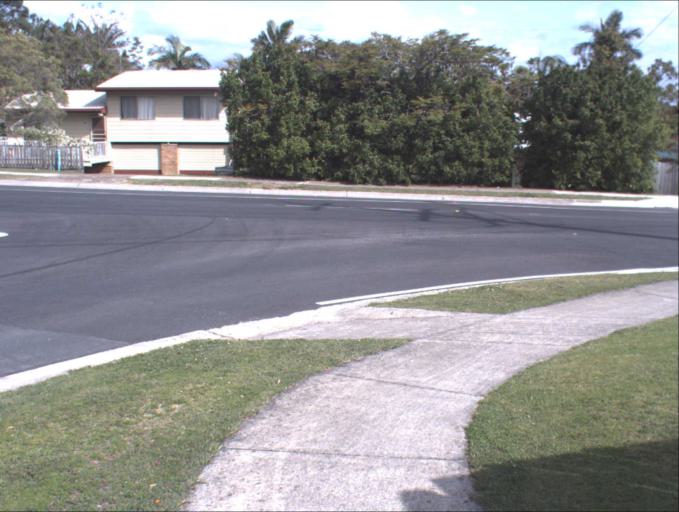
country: AU
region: Queensland
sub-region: Logan
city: Waterford West
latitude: -27.6857
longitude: 153.1196
